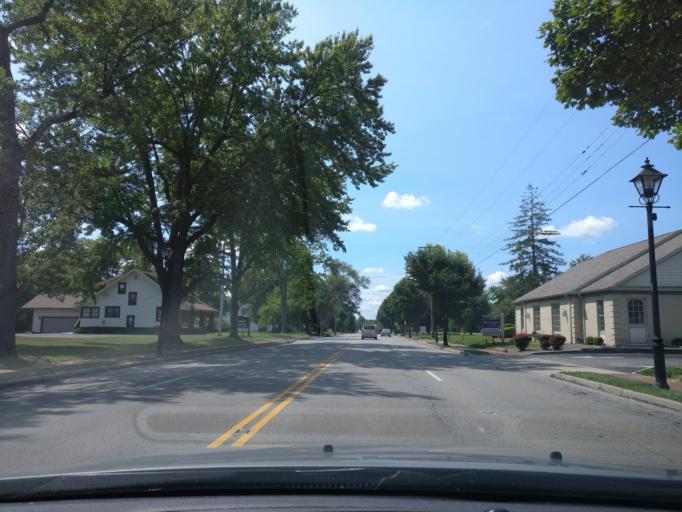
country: US
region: Ohio
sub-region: Montgomery County
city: Centerville
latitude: 39.6257
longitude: -84.1592
